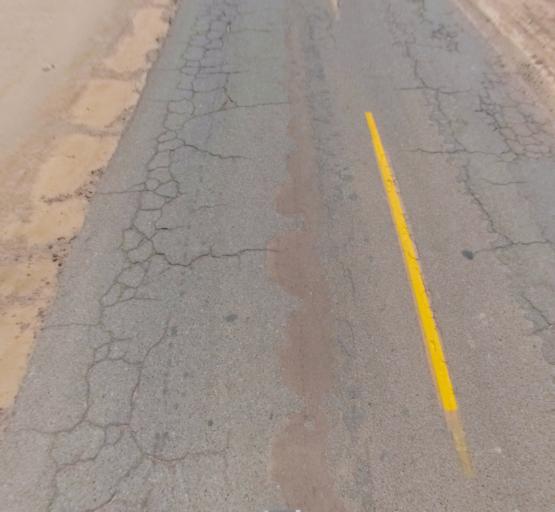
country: US
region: California
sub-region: Madera County
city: Bonadelle Ranchos-Madera Ranchos
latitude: 36.8949
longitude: -119.8508
